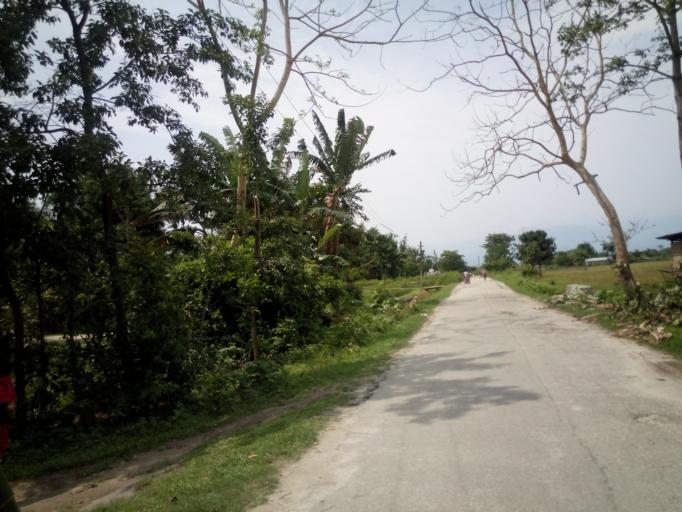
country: IN
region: Assam
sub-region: Udalguri
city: Udalguri
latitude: 26.7359
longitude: 92.1430
